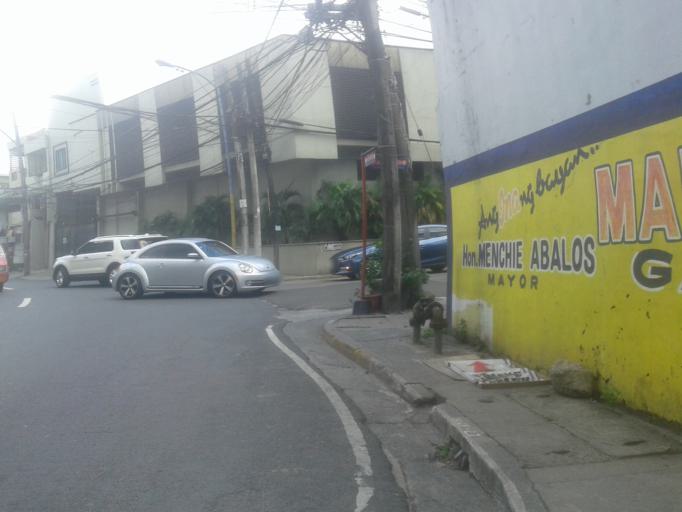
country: PH
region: Metro Manila
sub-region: Mandaluyong
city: Mandaluyong City
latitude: 14.5876
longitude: 121.0399
